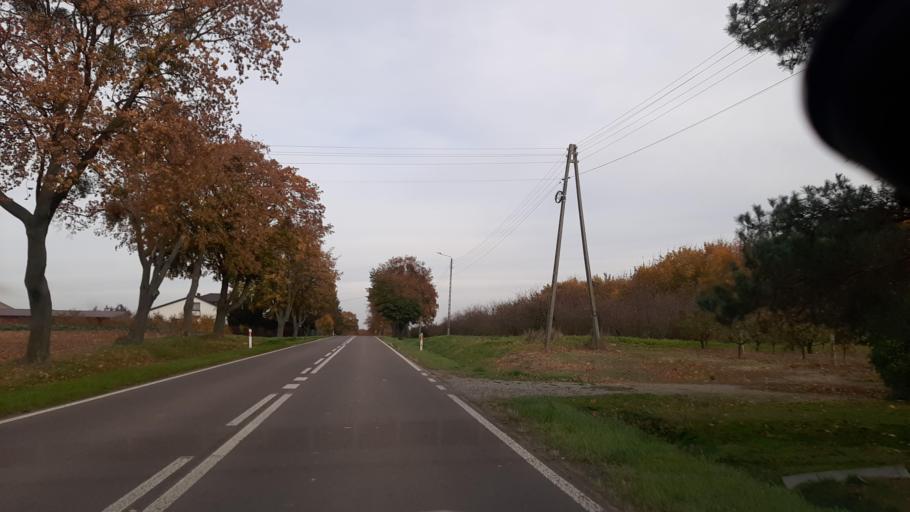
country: PL
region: Lublin Voivodeship
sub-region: Powiat pulawski
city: Markuszow
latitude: 51.3522
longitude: 22.2723
